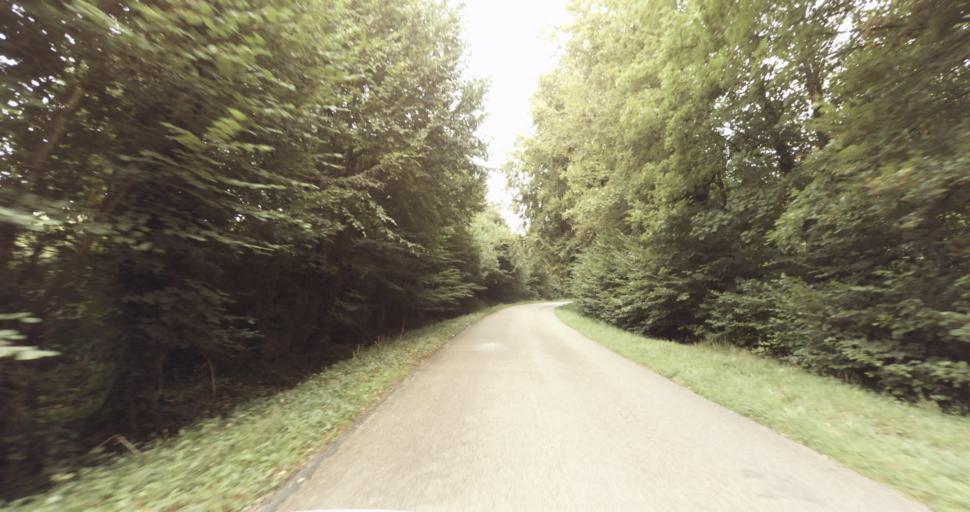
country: FR
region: Lower Normandy
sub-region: Departement de l'Orne
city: Vimoutiers
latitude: 48.9280
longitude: 0.1822
